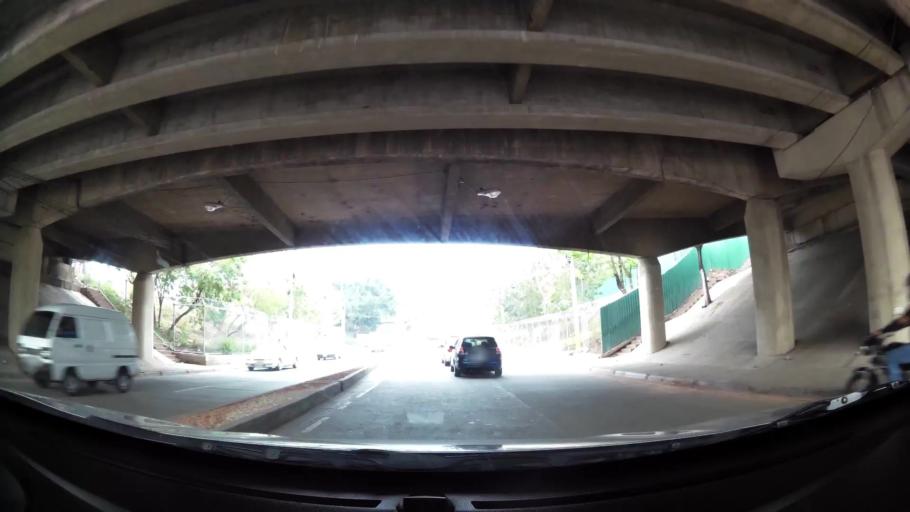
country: HN
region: Francisco Morazan
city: Tegucigalpa
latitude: 14.0884
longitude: -87.1956
